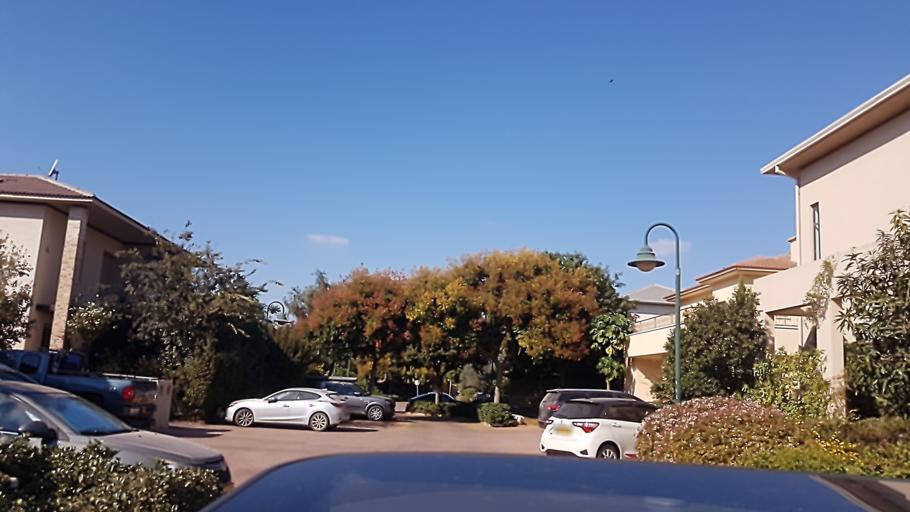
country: IL
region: Central District
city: Ra'anana
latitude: 32.2130
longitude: 34.8955
